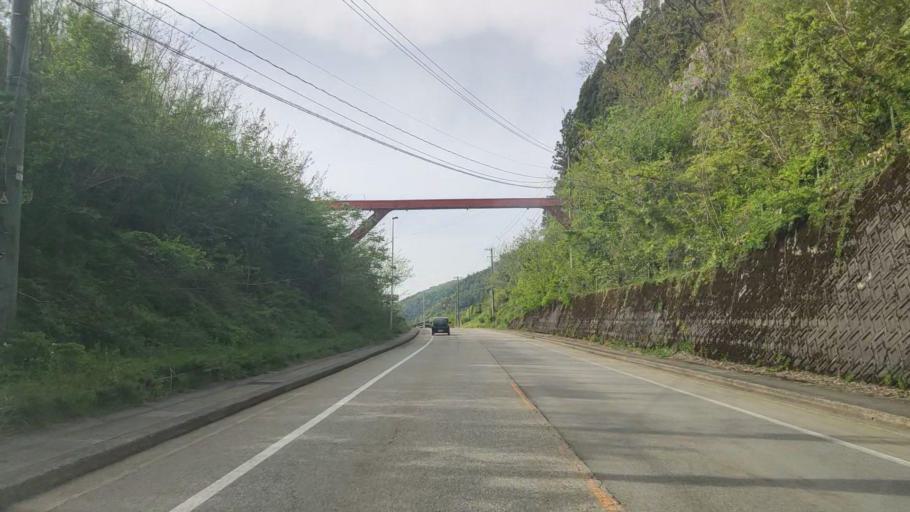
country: JP
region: Gifu
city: Takayama
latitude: 36.3214
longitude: 137.3117
